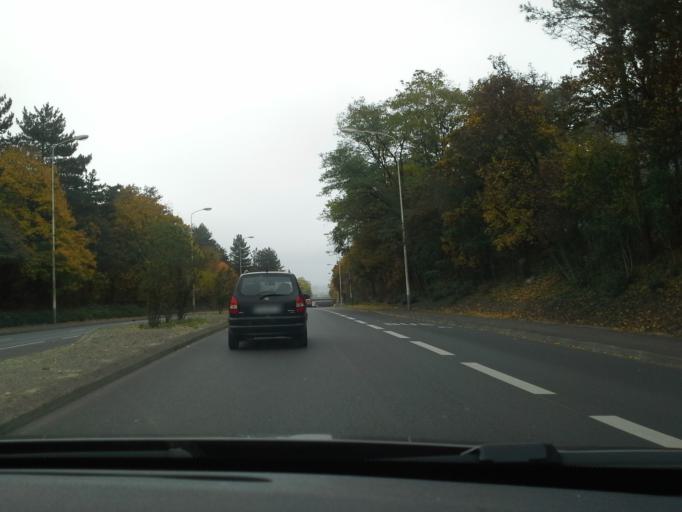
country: FR
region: Centre
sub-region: Departement d'Indre-et-Loire
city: Tours
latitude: 47.4085
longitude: 0.7033
